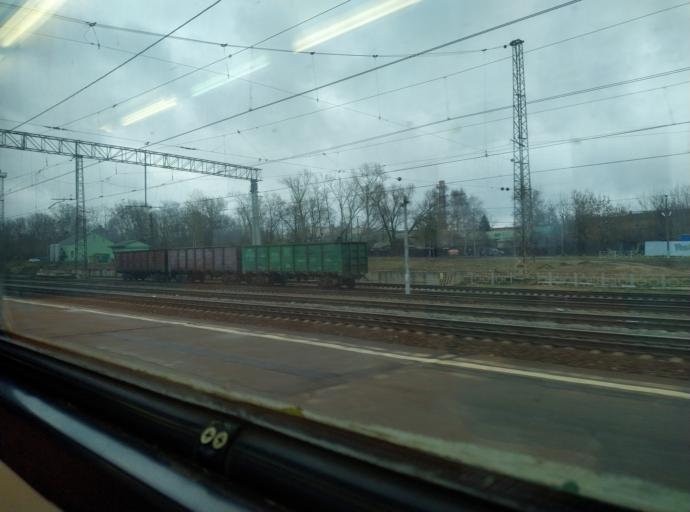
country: RU
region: Moskovskaya
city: Tomilino
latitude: 55.6727
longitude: 37.9316
